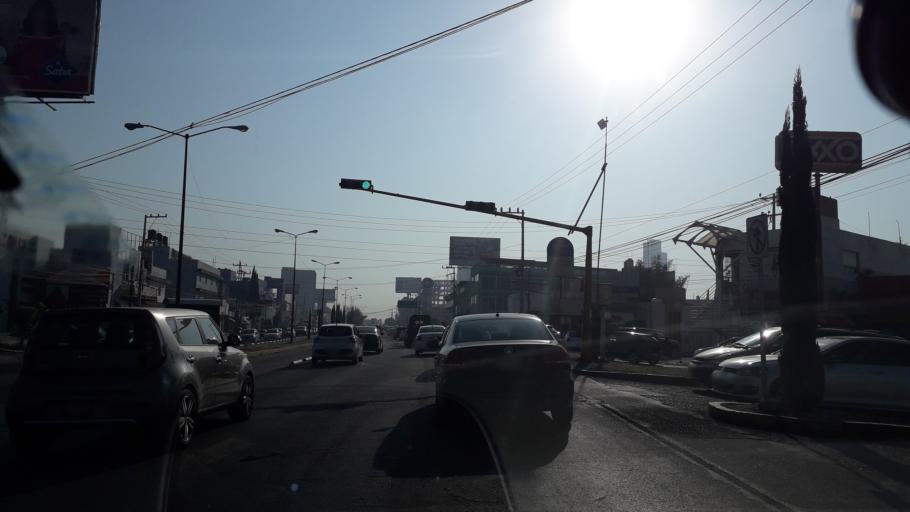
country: MX
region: Puebla
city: Tlazcalancingo
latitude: 19.0364
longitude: -98.2499
